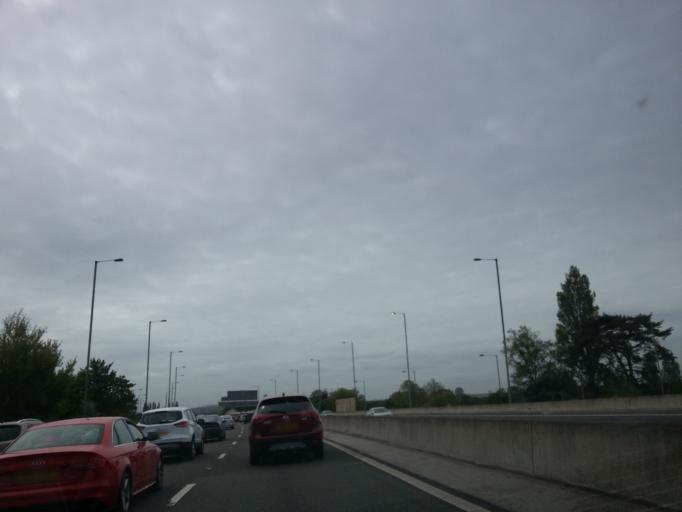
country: GB
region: England
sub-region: Cheshire West and Chester
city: Shotwick
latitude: 53.2223
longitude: -2.9990
